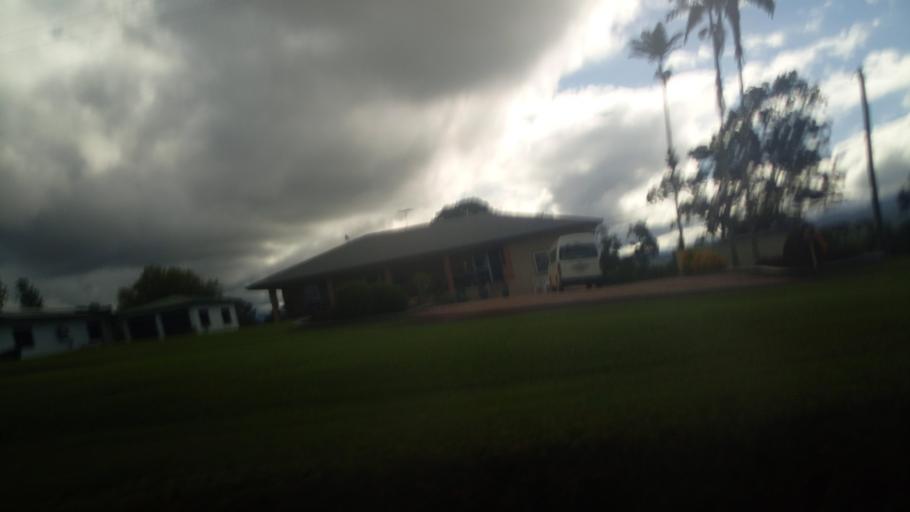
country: AU
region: Queensland
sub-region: Cassowary Coast
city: Innisfail
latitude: -17.5494
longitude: 145.9646
